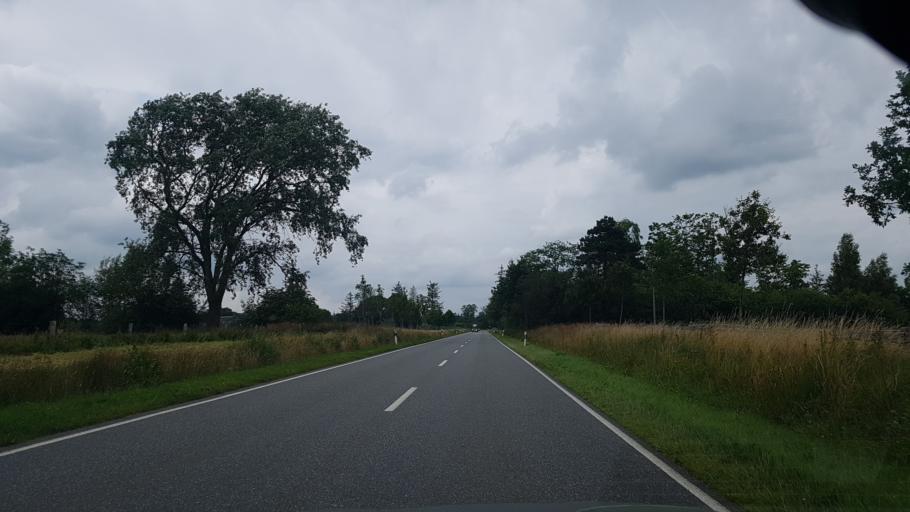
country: DE
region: Schleswig-Holstein
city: Osterby
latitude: 54.8165
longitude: 9.2270
